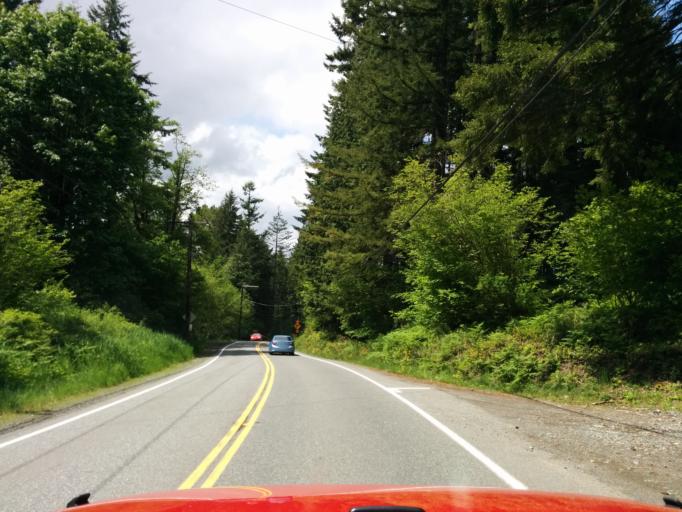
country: US
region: Washington
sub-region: King County
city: Riverbend
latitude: 47.4510
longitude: -121.7583
